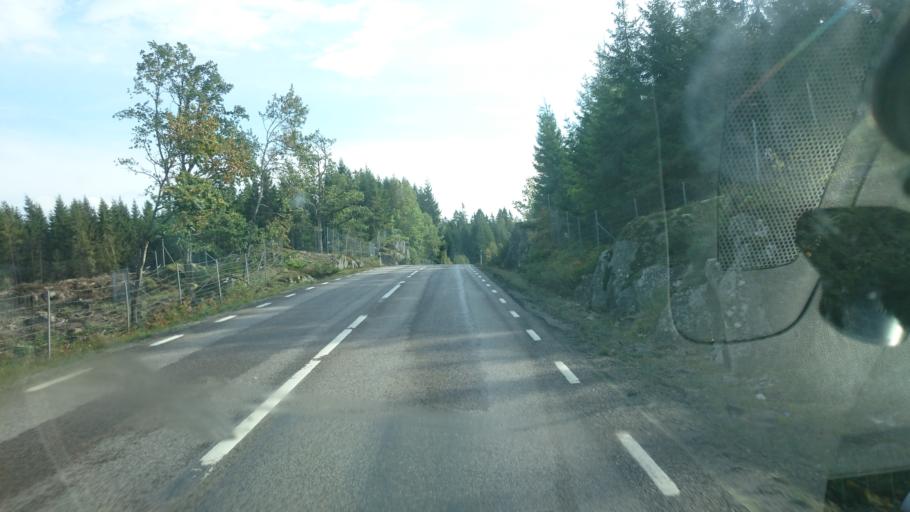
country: SE
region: Vaestra Goetaland
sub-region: Alingsas Kommun
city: Sollebrunn
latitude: 58.1357
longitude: 12.4617
